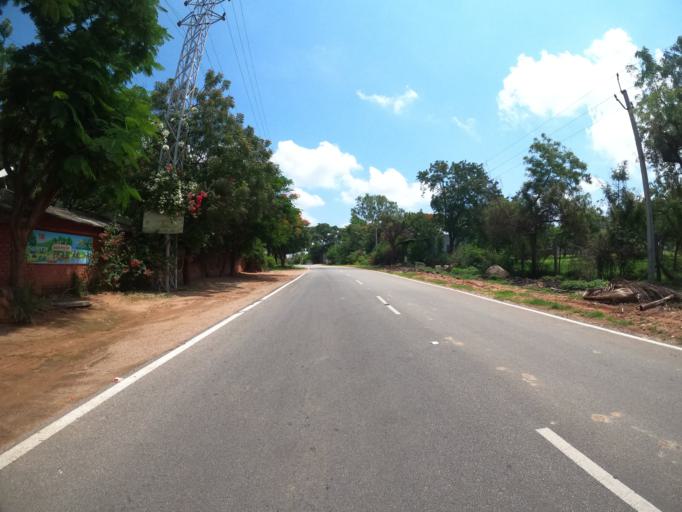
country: IN
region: Telangana
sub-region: Rangareddi
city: Sriramnagar
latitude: 17.3687
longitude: 78.3251
